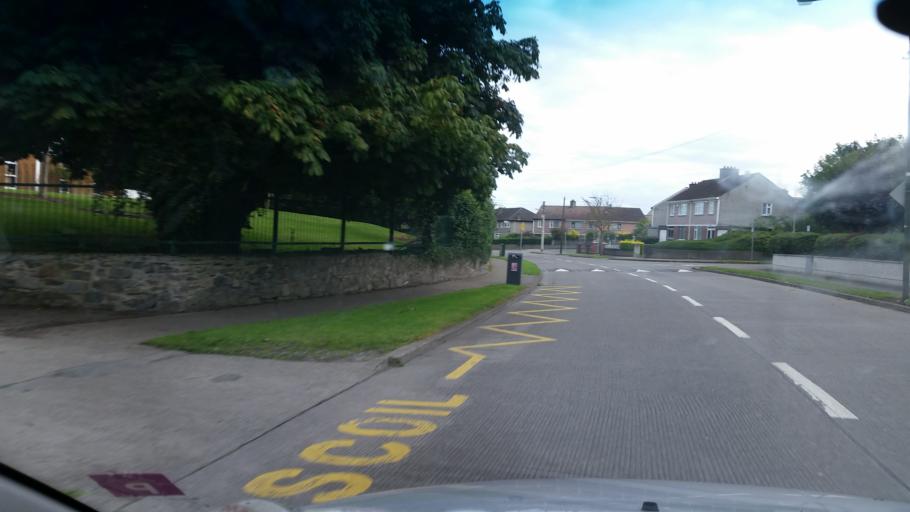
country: IE
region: Leinster
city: Glasnevin
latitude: 53.3854
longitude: -6.2785
